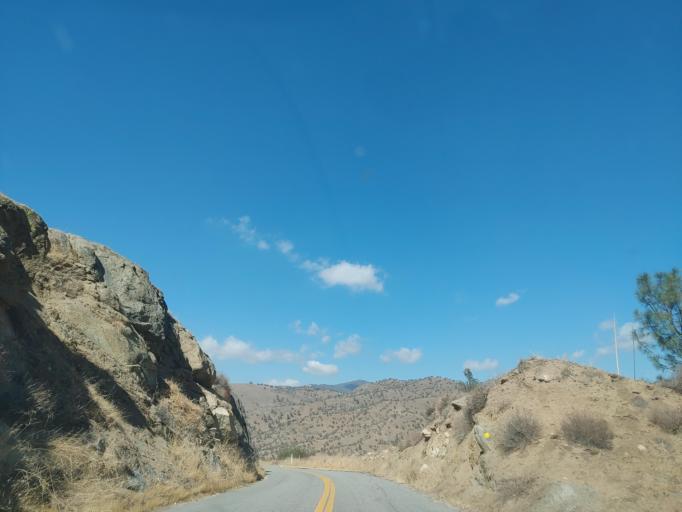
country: US
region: California
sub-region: Kern County
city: Golden Hills
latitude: 35.1903
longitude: -118.5239
